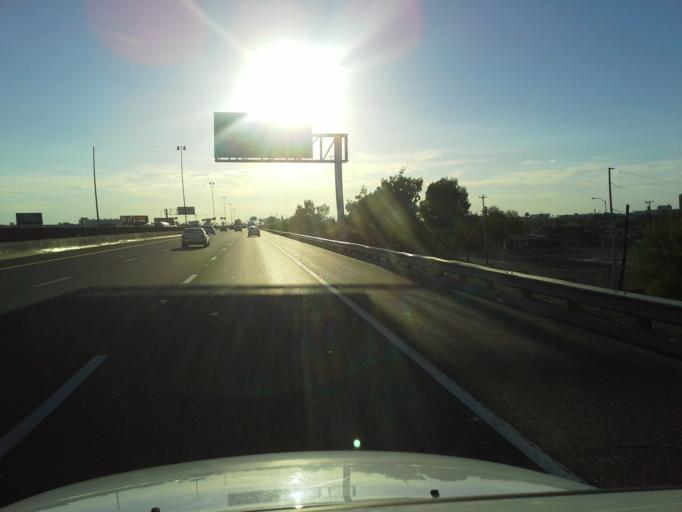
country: US
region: Arizona
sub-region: Maricopa County
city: Phoenix
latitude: 33.4281
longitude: -112.0551
